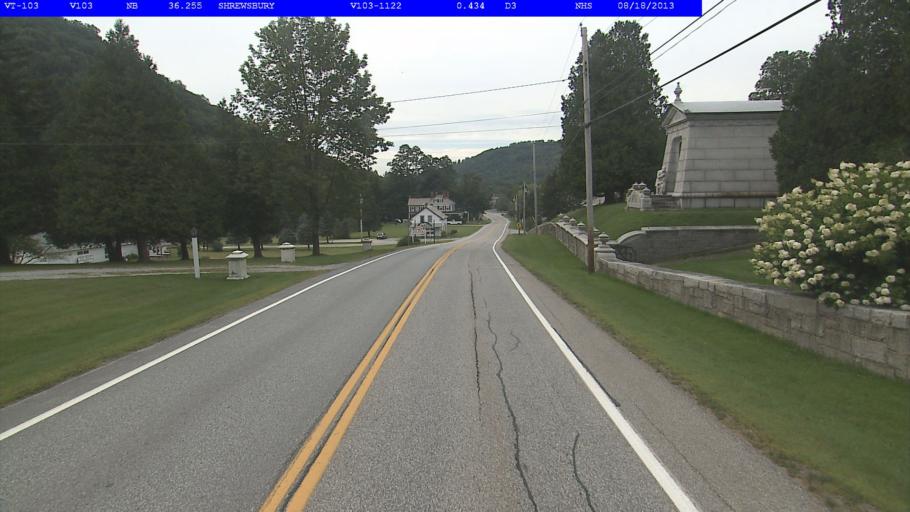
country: US
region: Vermont
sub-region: Rutland County
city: Rutland
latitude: 43.4795
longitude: -72.8945
